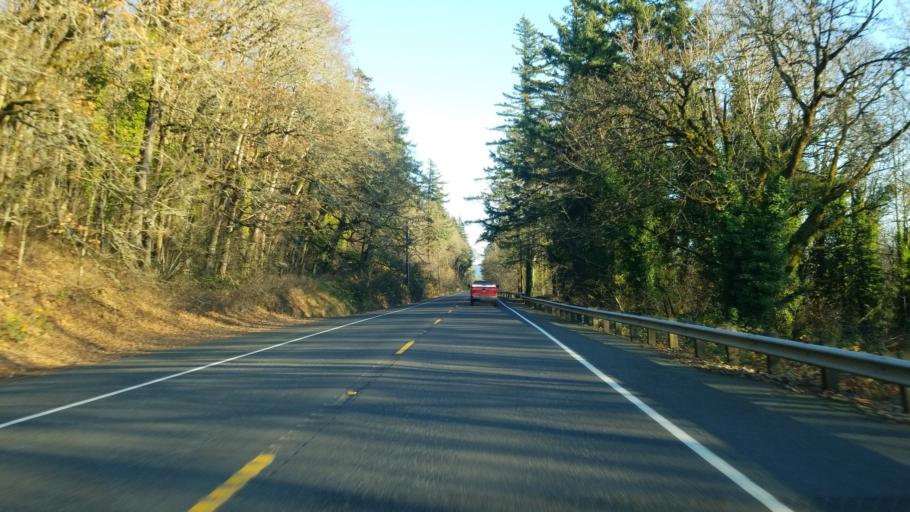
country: US
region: Washington
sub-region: Clark County
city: Washougal
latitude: 45.5688
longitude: -122.2908
